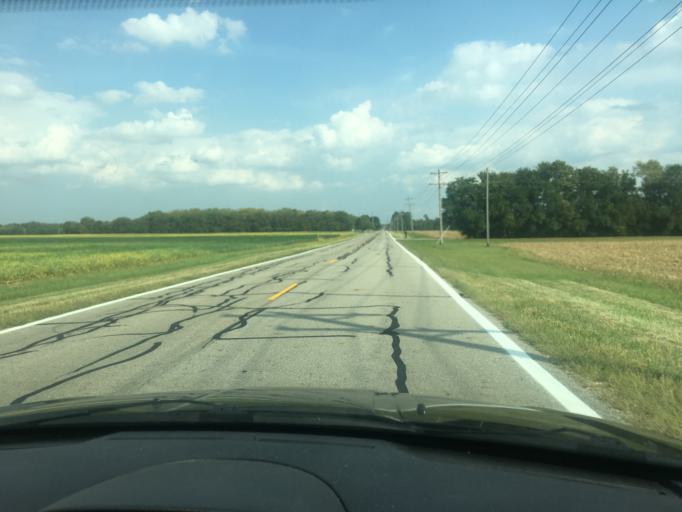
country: US
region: Ohio
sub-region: Champaign County
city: Urbana
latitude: 40.1306
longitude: -83.8197
